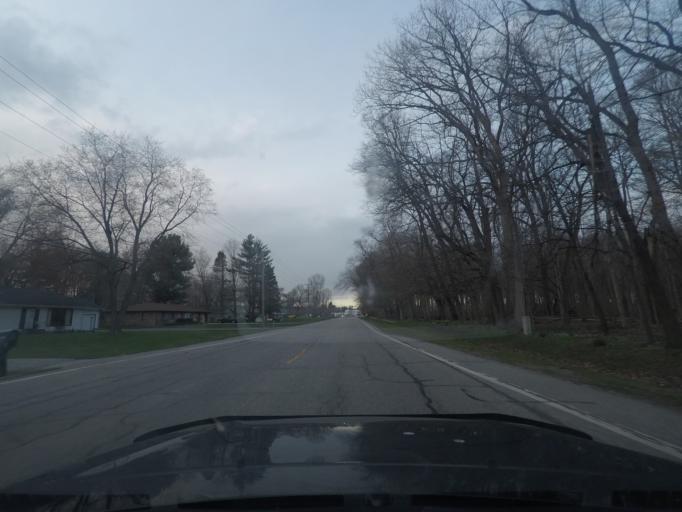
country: US
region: Indiana
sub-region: LaPorte County
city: LaPorte
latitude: 41.5961
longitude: -86.7392
